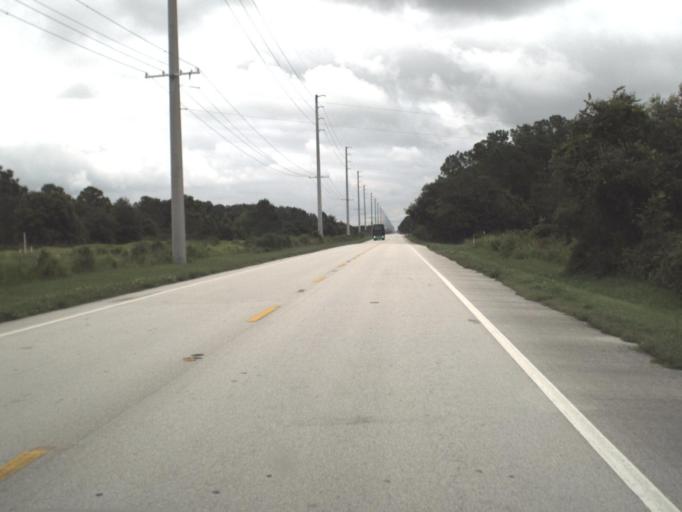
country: US
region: Florida
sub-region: Hardee County
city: Bowling Green
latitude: 27.5951
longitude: -82.0349
